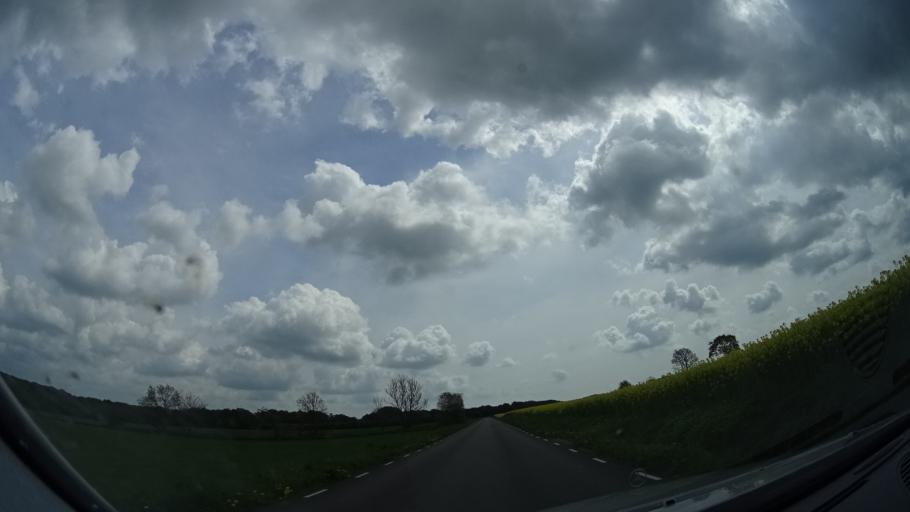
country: SE
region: Skane
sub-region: Hoors Kommun
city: Loberod
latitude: 55.7965
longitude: 13.4871
